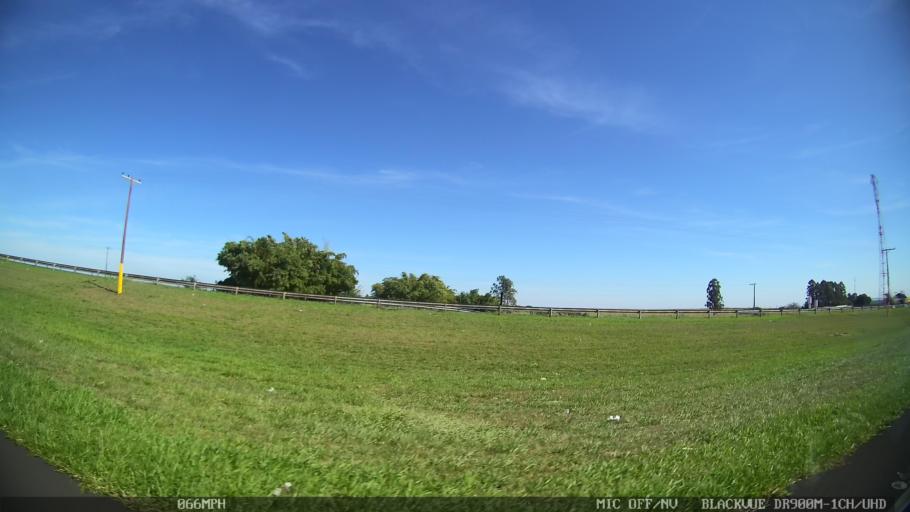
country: BR
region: Sao Paulo
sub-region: Santa Rita Do Passa Quatro
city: Santa Rita do Passa Quatro
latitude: -21.6812
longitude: -47.6029
